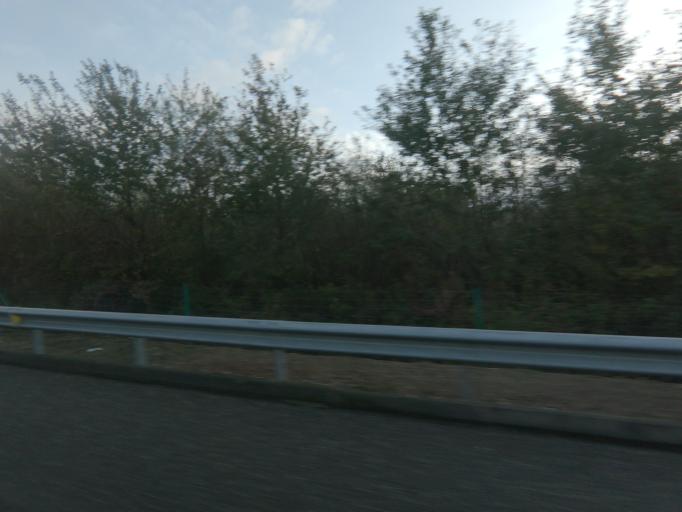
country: ES
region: Galicia
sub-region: Provincia de Pontevedra
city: Porrino
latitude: 42.1084
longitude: -8.6503
